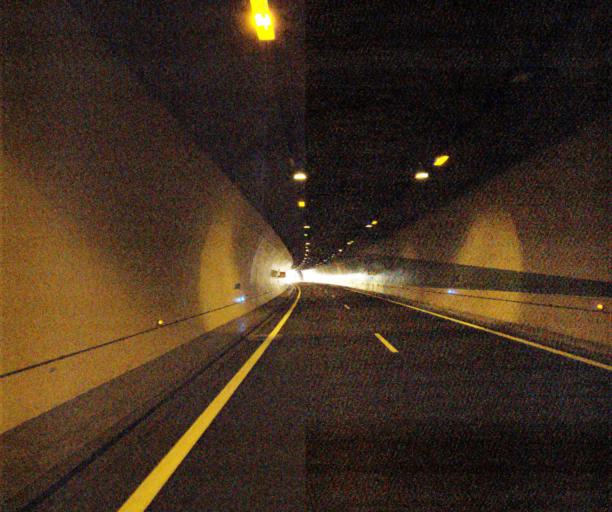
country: FR
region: Rhone-Alpes
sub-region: Departement de l'Isere
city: Vif
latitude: 45.0526
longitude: 5.6861
